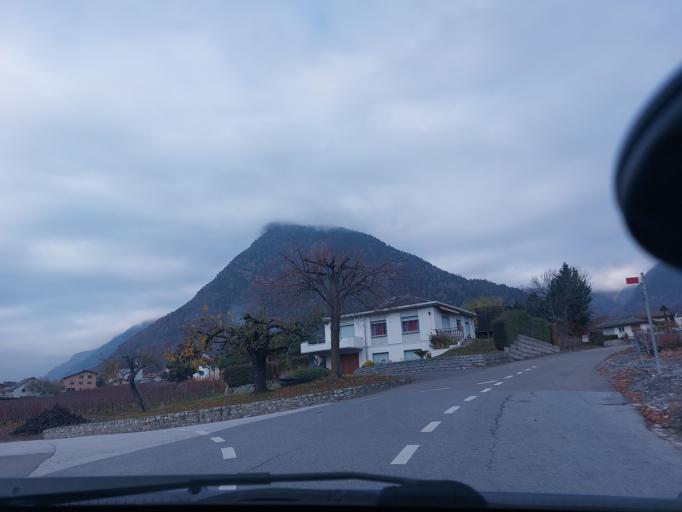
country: CH
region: Valais
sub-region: Conthey District
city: Chamoson
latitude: 46.2014
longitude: 7.2298
